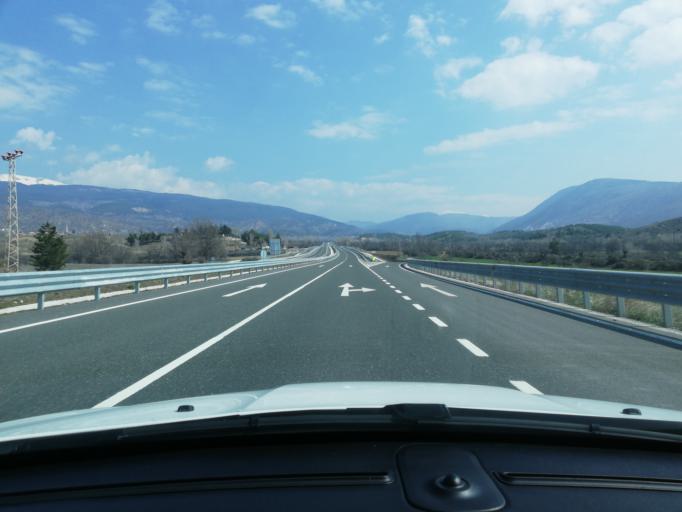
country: TR
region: Cankiri
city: Ilgaz
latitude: 40.9326
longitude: 33.6531
